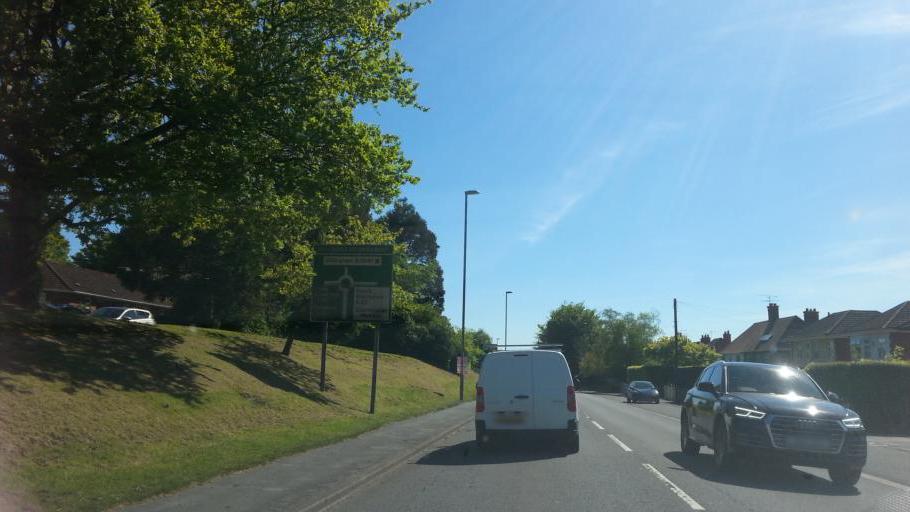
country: GB
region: England
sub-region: Dorset
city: Shaftesbury
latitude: 51.0119
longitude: -2.1919
